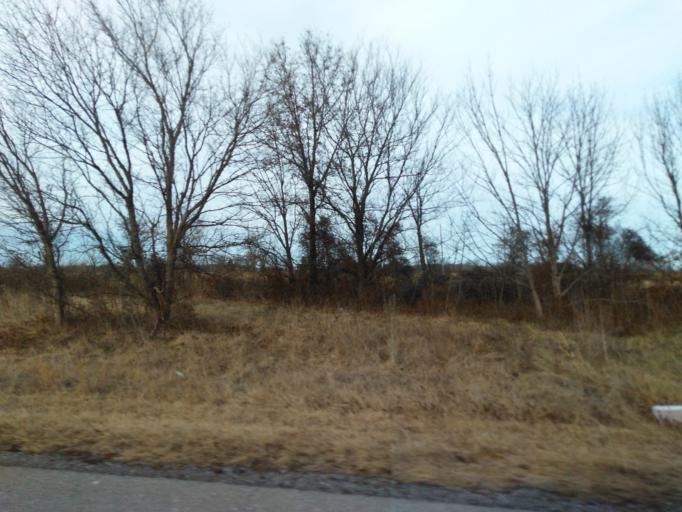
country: US
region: Illinois
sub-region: Jefferson County
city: Mount Vernon
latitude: 38.3544
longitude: -88.9937
